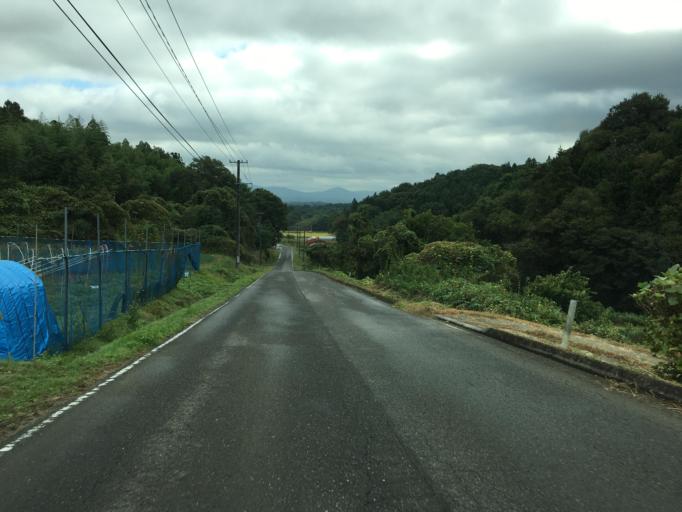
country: JP
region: Fukushima
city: Nihommatsu
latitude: 37.6291
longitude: 140.4391
